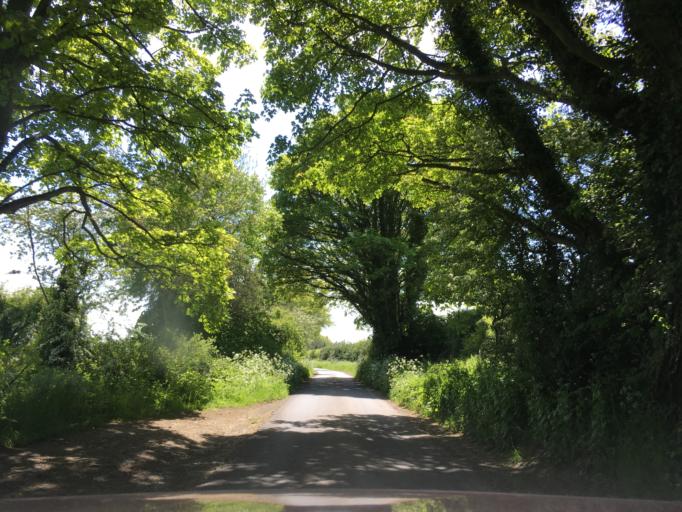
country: GB
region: England
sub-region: Gloucestershire
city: Brimscombe
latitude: 51.7393
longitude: -2.1826
